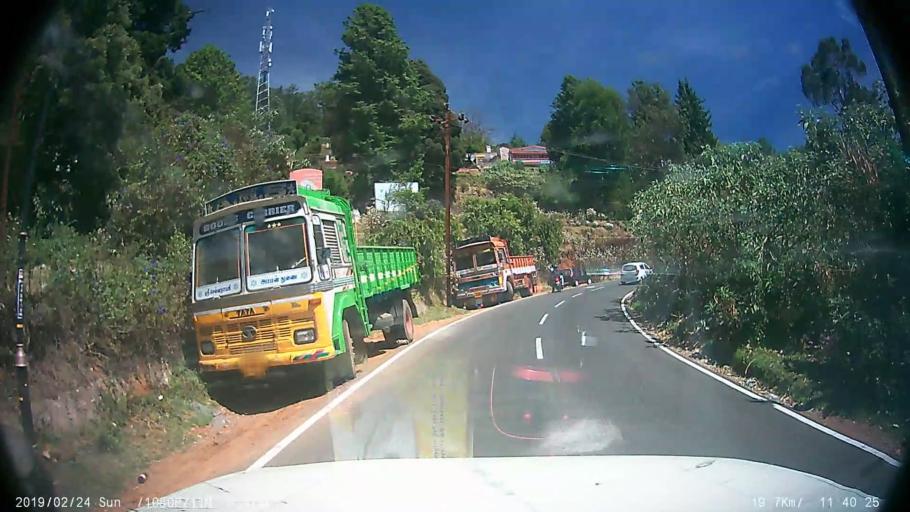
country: IN
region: Tamil Nadu
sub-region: Nilgiri
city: Ooty
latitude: 11.4151
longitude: 76.7026
